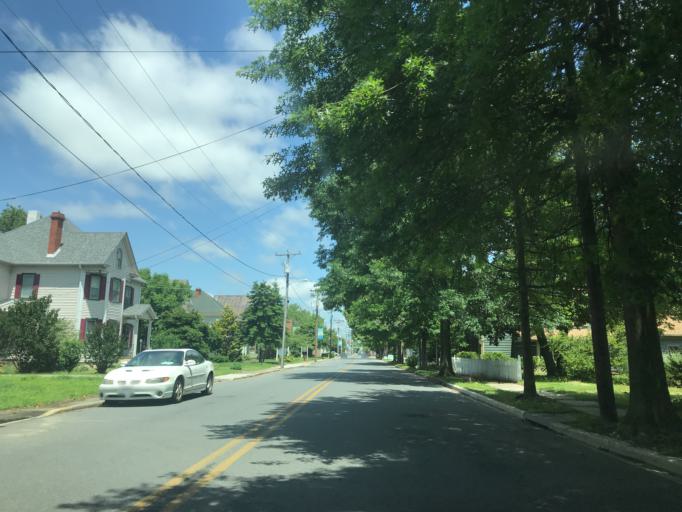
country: US
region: Maryland
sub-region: Caroline County
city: Federalsburg
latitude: 38.6903
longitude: -75.7725
